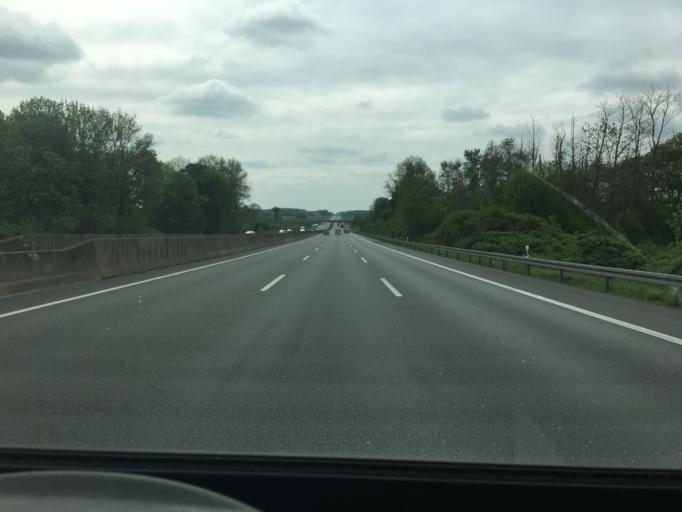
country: DE
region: North Rhine-Westphalia
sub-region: Regierungsbezirk Munster
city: Beckum
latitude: 51.7654
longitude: 8.0048
